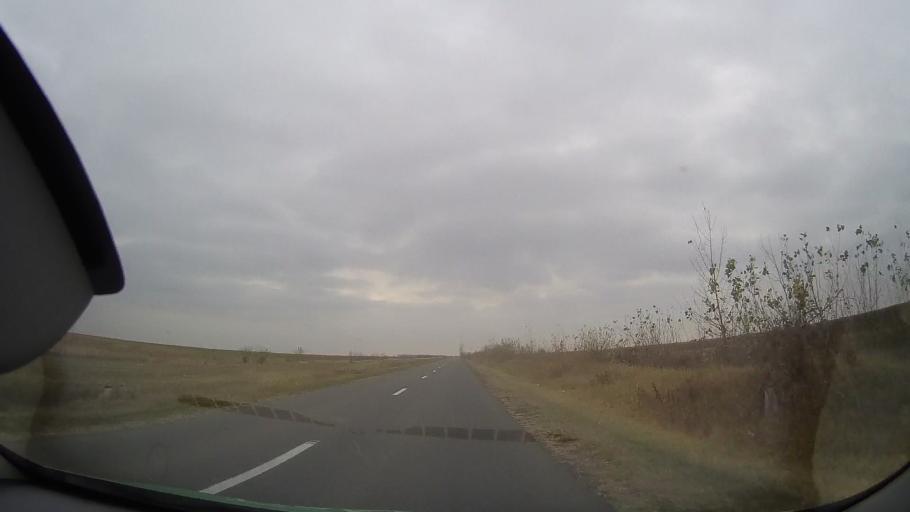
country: RO
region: Ialomita
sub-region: Comuna Garbovi
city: Garbovi
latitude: 44.7680
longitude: 26.7405
